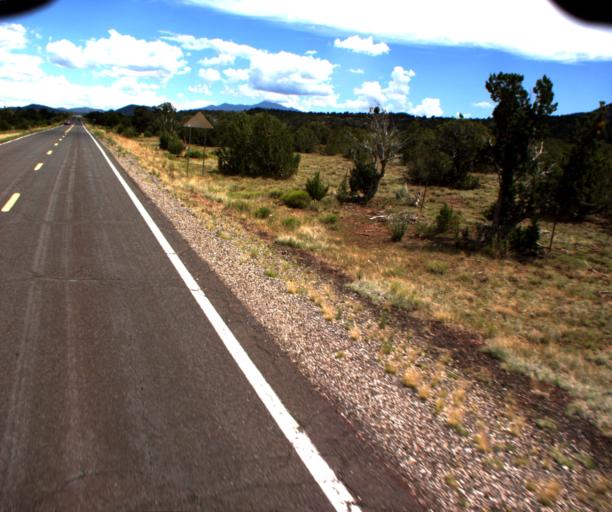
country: US
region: Arizona
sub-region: Coconino County
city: Parks
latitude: 35.5609
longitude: -111.8807
